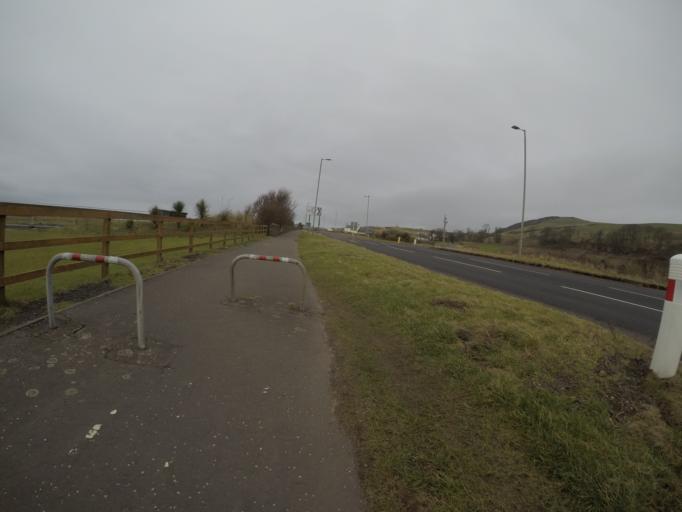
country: GB
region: Scotland
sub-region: North Ayrshire
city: West Kilbride
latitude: 55.6755
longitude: -4.8527
